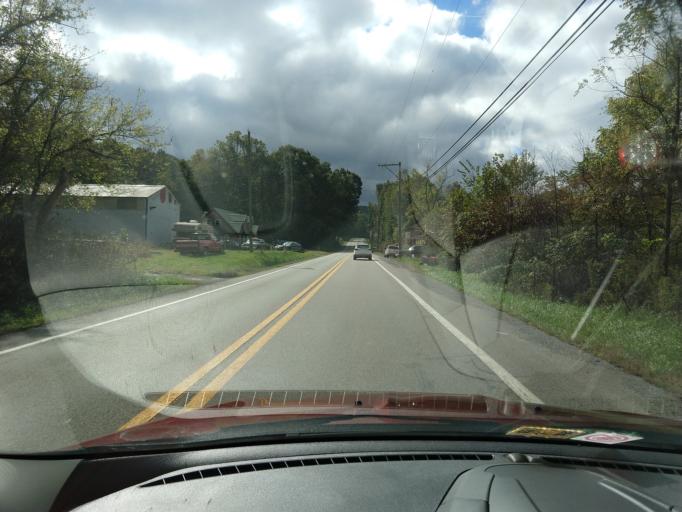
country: US
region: West Virginia
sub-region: Barbour County
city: Belington
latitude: 38.9952
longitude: -79.9360
